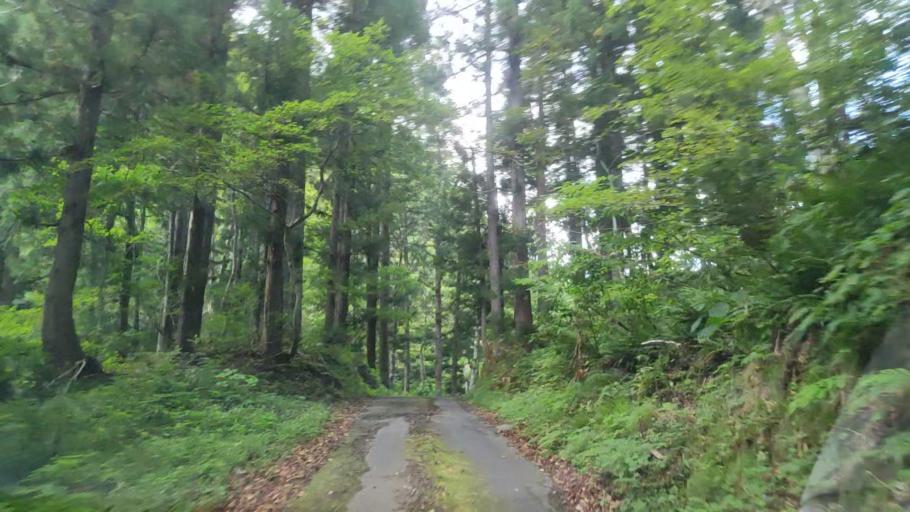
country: JP
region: Gifu
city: Takayama
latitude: 36.3182
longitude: 137.0837
